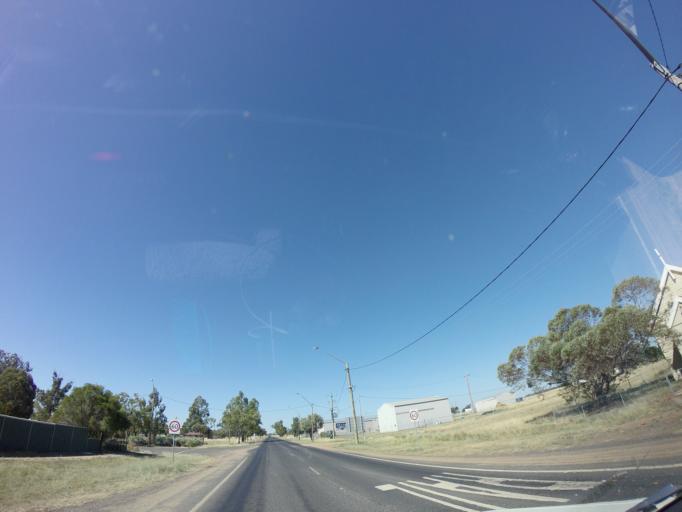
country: AU
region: New South Wales
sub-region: Bogan
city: Nyngan
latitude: -31.8378
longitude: 147.7196
